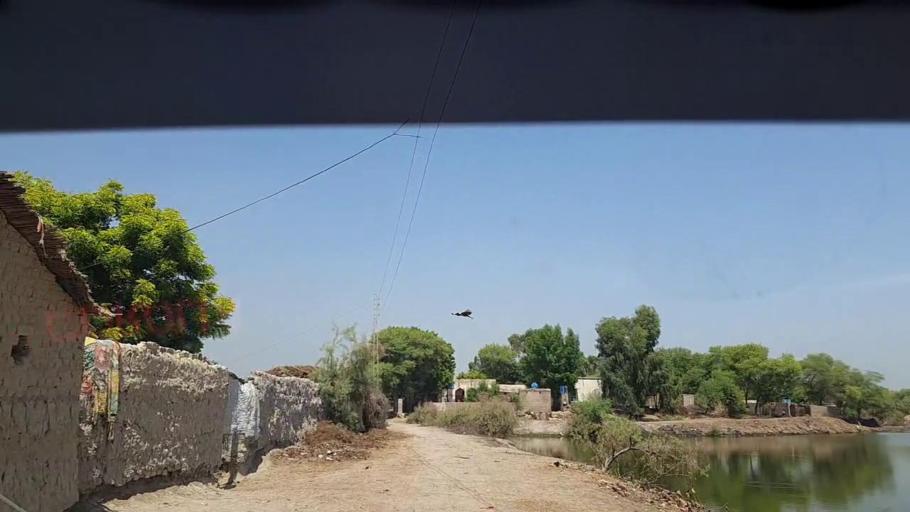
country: PK
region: Sindh
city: Ghauspur
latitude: 28.1644
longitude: 69.1433
